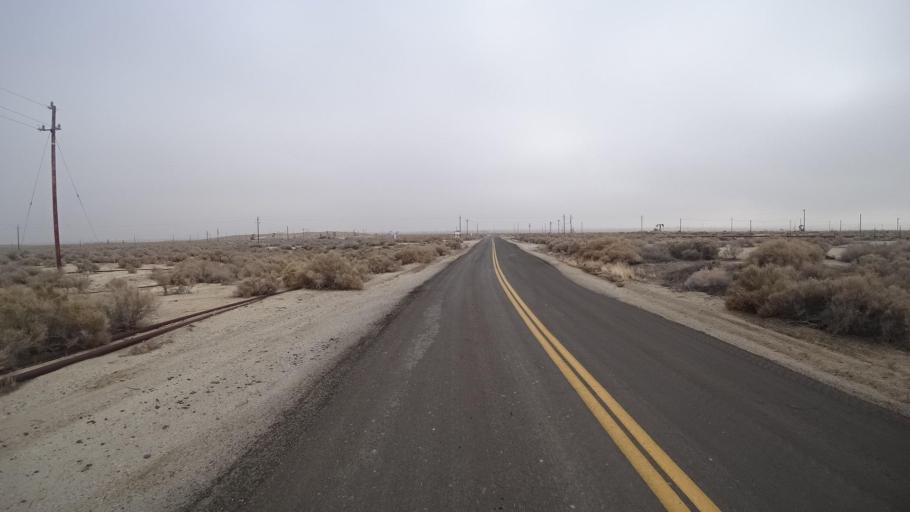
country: US
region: California
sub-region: Kern County
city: Maricopa
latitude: 35.0770
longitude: -119.3688
